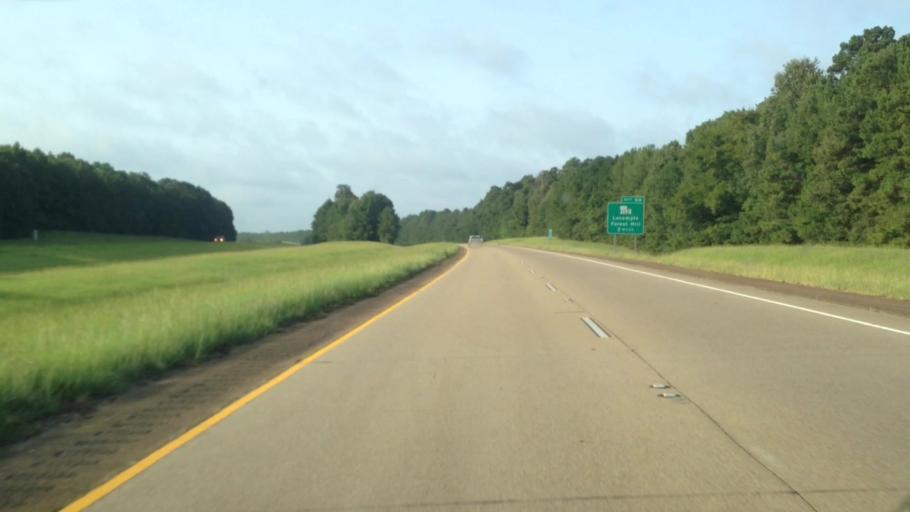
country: US
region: Louisiana
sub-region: Rapides Parish
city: Lecompte
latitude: 31.1032
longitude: -92.4454
